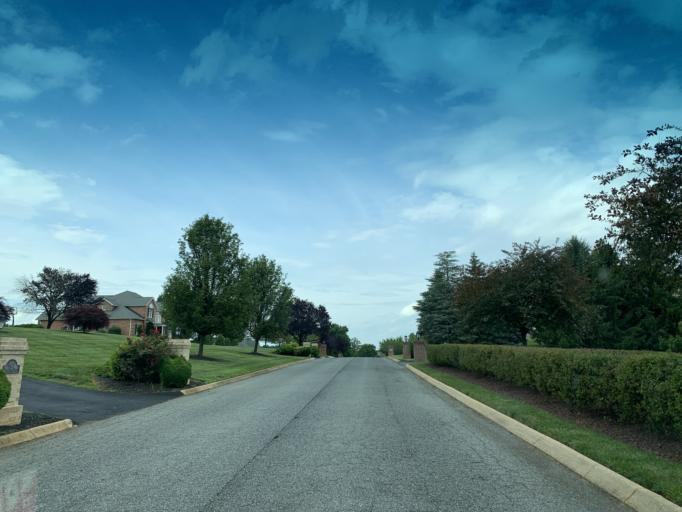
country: US
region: Maryland
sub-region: Harford County
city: Fallston
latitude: 39.5283
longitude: -76.4219
